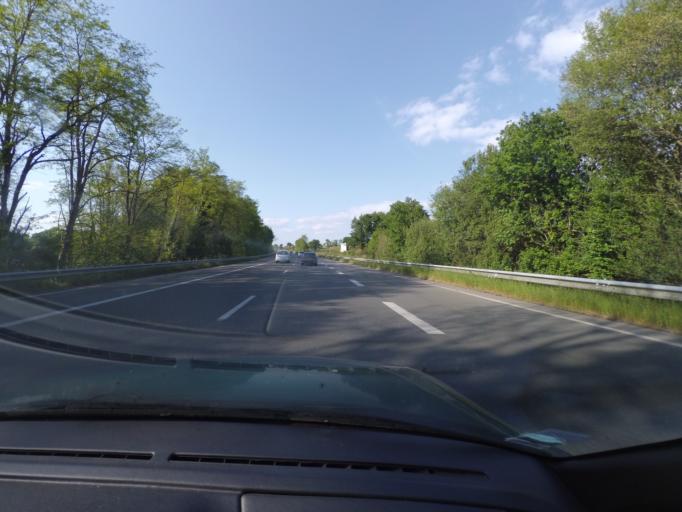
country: FR
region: Pays de la Loire
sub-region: Departement de la Vendee
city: Aubigny
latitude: 46.5956
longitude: -1.4429
